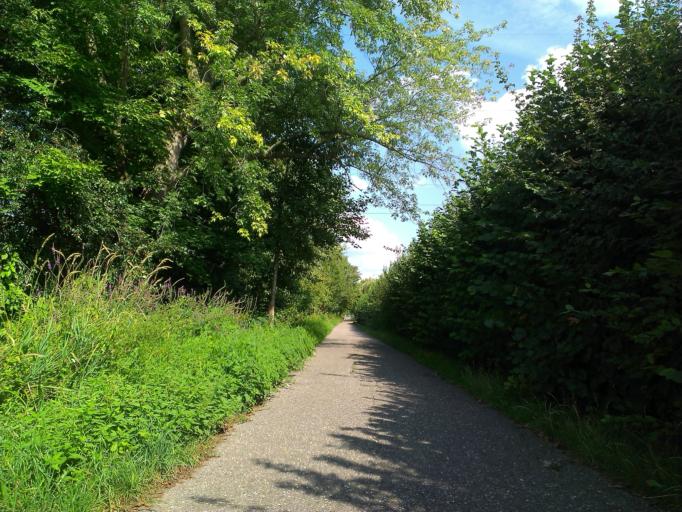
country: DE
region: Baden-Wuerttemberg
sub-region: Karlsruhe Region
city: Ladenburg
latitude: 49.4723
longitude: 8.6322
